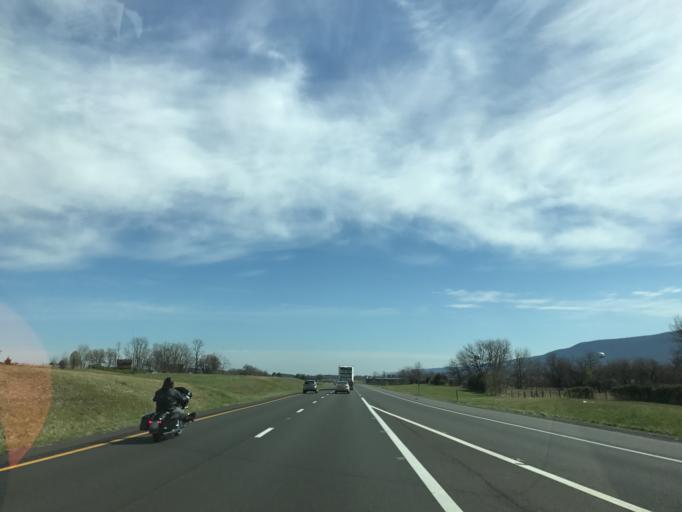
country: US
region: Virginia
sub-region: Shenandoah County
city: Mount Jackson
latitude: 38.7640
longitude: -78.6311
